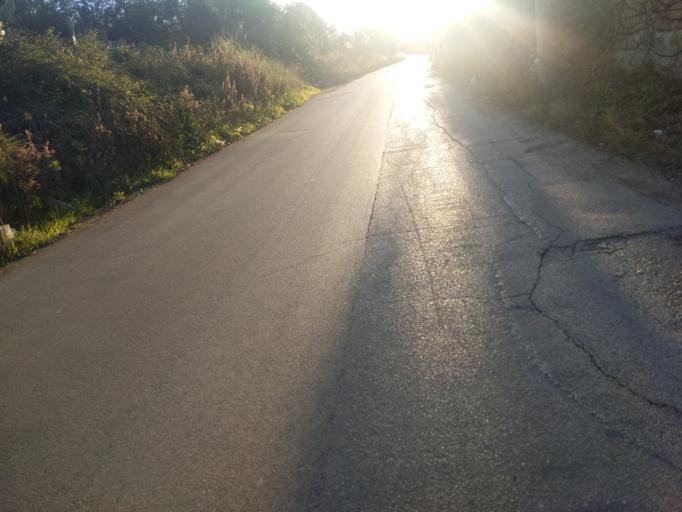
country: IT
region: Apulia
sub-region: Provincia di Bari
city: Bari
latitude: 41.1090
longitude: 16.8370
